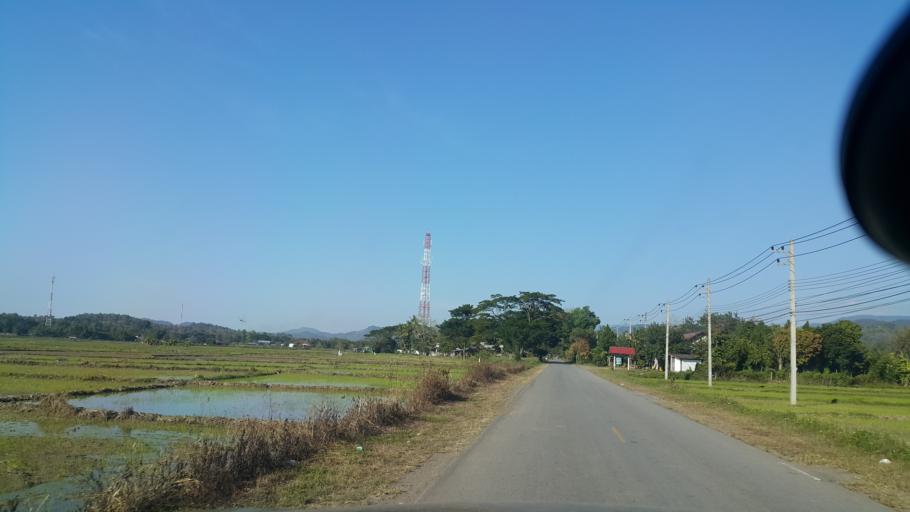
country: TH
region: Chiang Mai
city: Mae On
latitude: 18.7769
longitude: 99.2545
